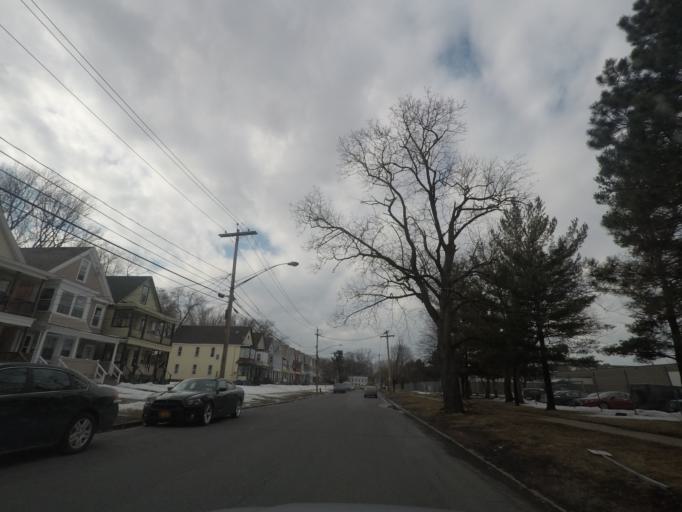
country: US
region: New York
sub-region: Albany County
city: West Albany
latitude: 42.6730
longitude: -73.7745
